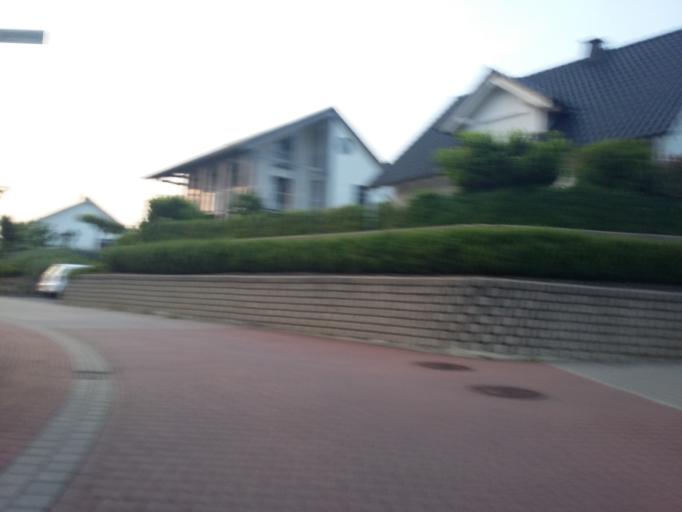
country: DE
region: North Rhine-Westphalia
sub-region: Regierungsbezirk Detmold
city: Vlotho
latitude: 52.1792
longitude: 8.8747
